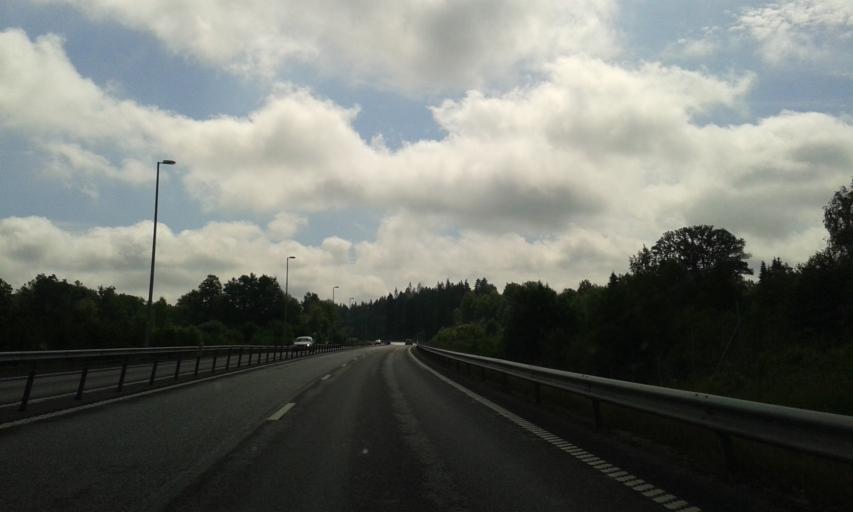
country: SE
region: Vaestra Goetaland
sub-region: Boras Kommun
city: Ganghester
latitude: 57.6792
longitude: 12.9699
